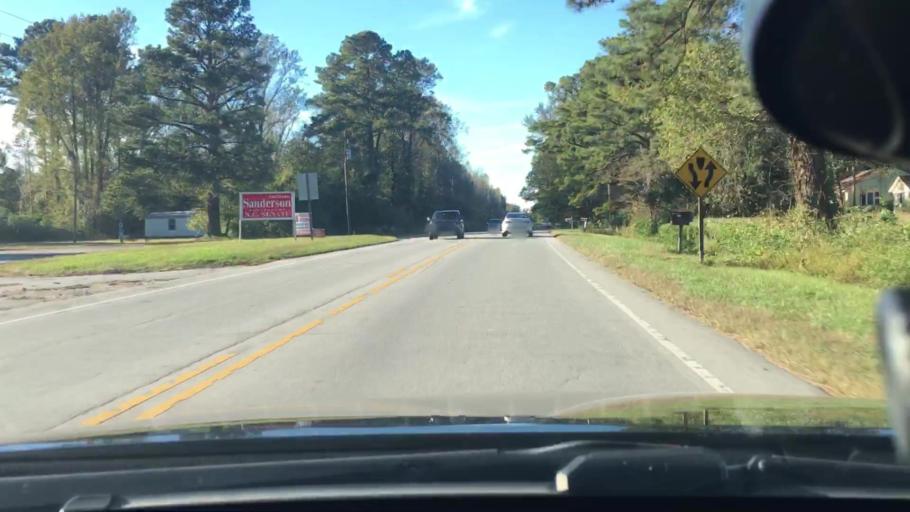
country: US
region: North Carolina
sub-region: Craven County
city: Vanceboro
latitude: 35.2802
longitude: -77.1221
